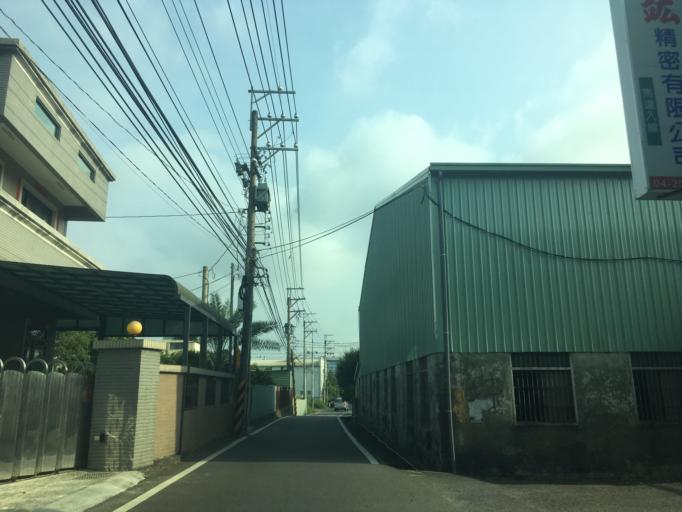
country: TW
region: Taiwan
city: Fengyuan
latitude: 24.2364
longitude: 120.7301
